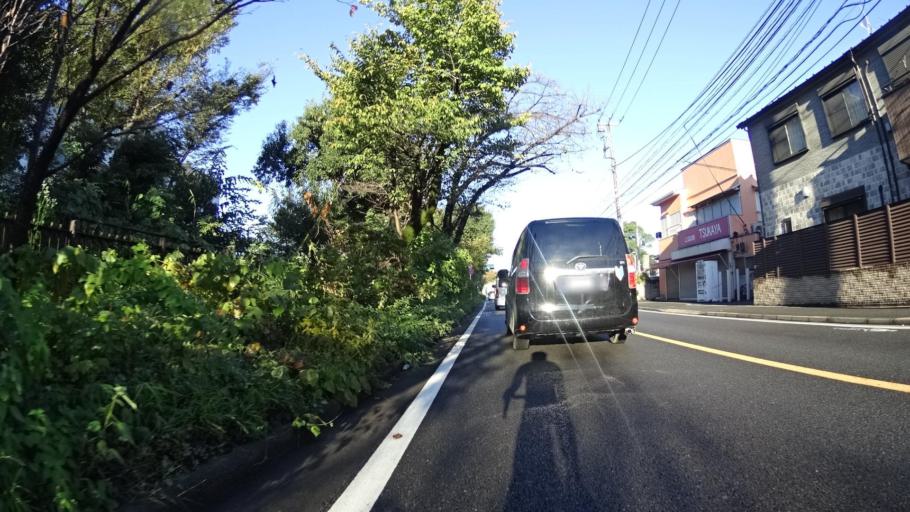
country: JP
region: Tokyo
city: Nishi-Tokyo-shi
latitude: 35.7116
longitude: 139.5346
